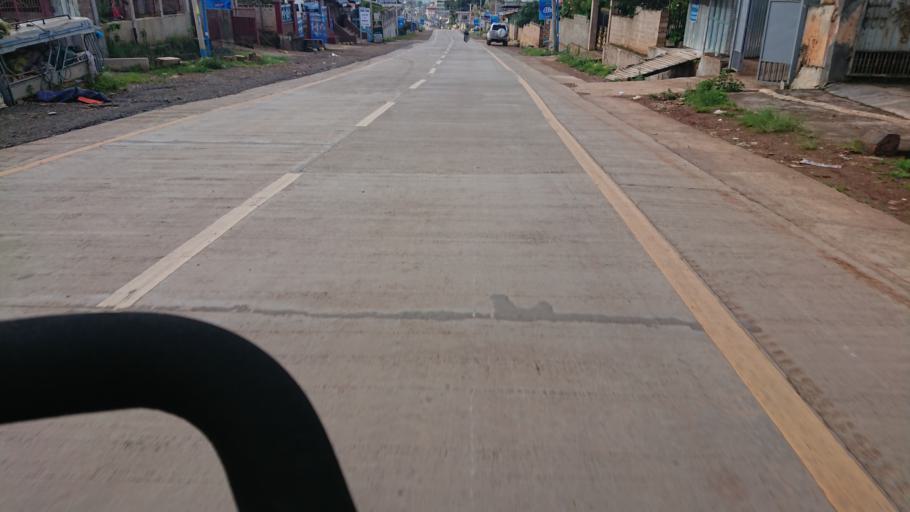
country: MM
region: Shan
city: Taunggyi
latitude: 20.7427
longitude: 97.0508
